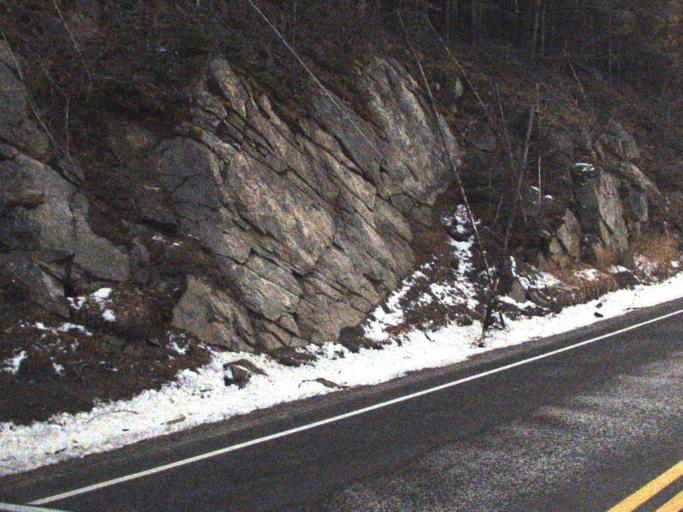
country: US
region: Washington
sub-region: Ferry County
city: Republic
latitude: 48.6043
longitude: -118.4989
